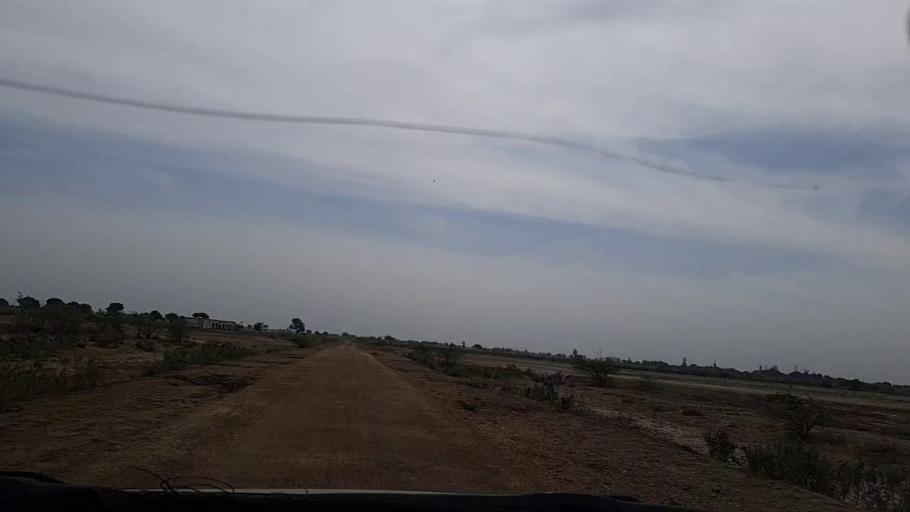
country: PK
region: Sindh
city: Dhoro Naro
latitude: 25.4512
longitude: 69.4910
